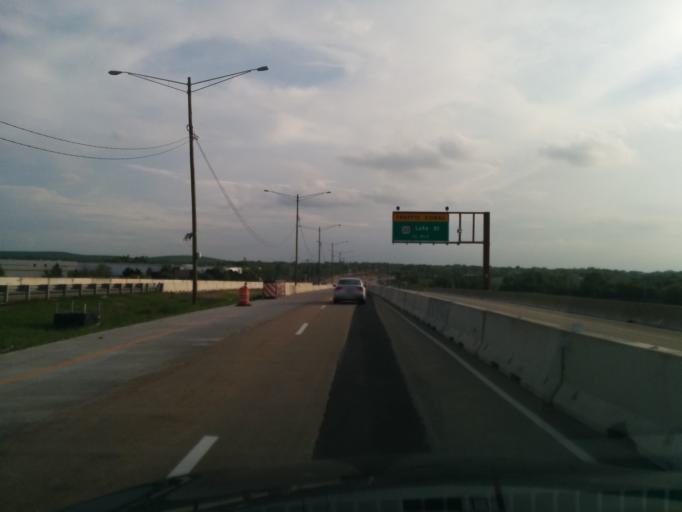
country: US
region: Illinois
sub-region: DuPage County
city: Hanover Park
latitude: 41.9883
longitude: -88.1286
